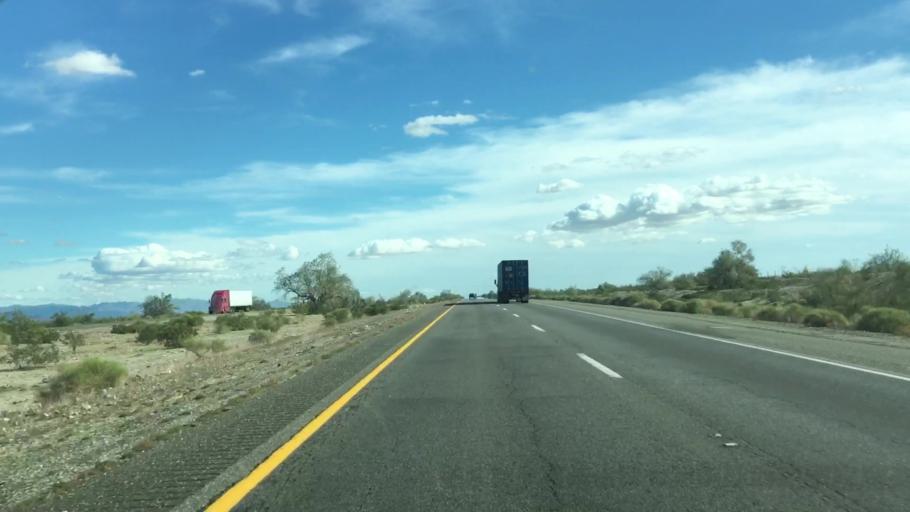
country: US
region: California
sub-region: Imperial County
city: Niland
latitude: 33.6982
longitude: -115.2975
